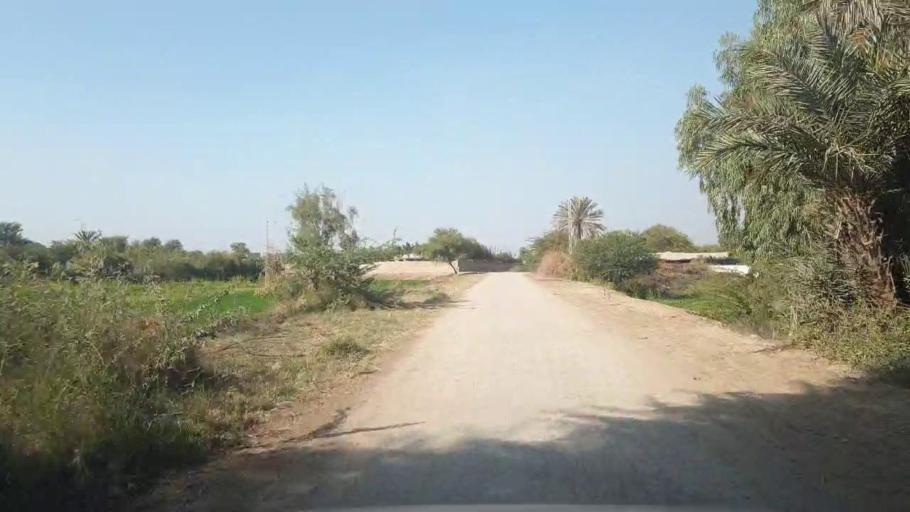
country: PK
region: Sindh
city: Chambar
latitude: 25.3156
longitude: 68.8420
